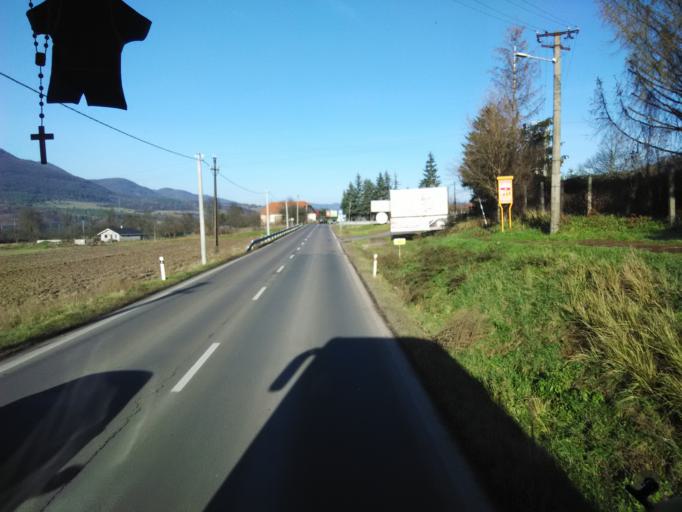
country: SK
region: Banskobystricky
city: Zarnovica
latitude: 48.5262
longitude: 18.7400
